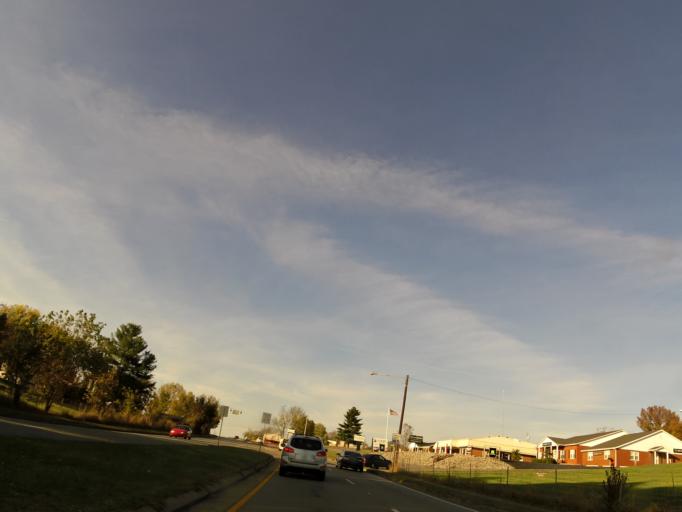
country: US
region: Kentucky
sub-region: Lincoln County
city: Stanford
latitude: 37.5314
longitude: -84.6526
